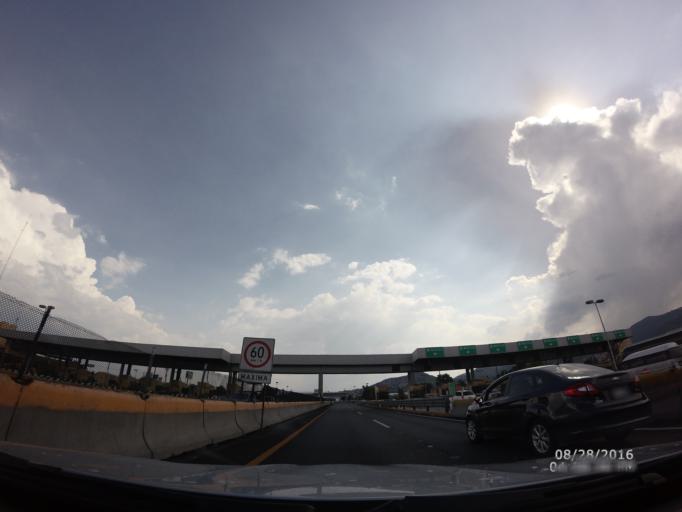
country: MX
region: Mexico
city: Ecatepec
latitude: 19.6031
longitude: -99.0379
